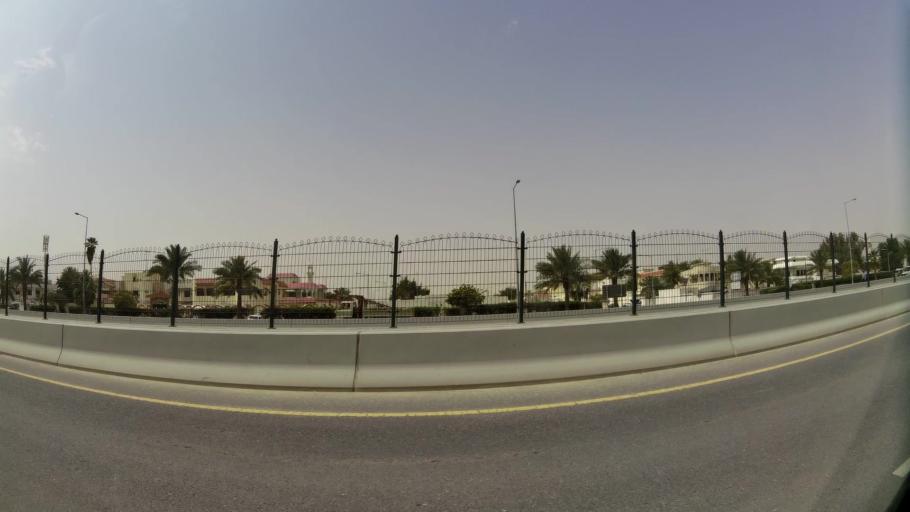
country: QA
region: Baladiyat ar Rayyan
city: Ar Rayyan
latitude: 25.2301
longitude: 51.4314
